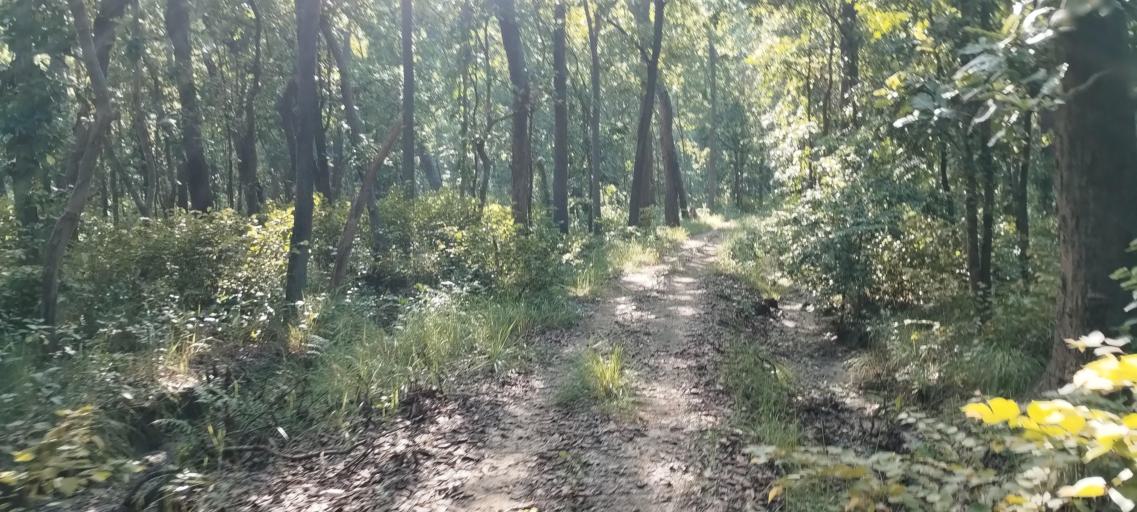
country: NP
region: Far Western
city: Tikapur
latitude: 28.5226
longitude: 81.2643
